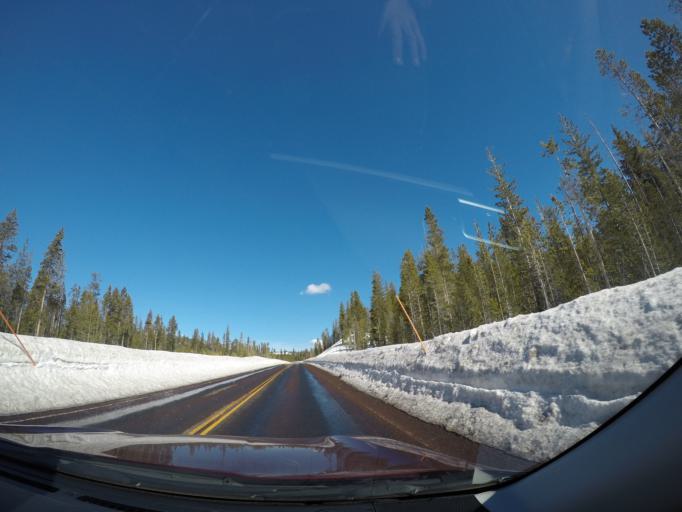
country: US
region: Oregon
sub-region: Deschutes County
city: Sunriver
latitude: 43.9593
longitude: -121.6156
